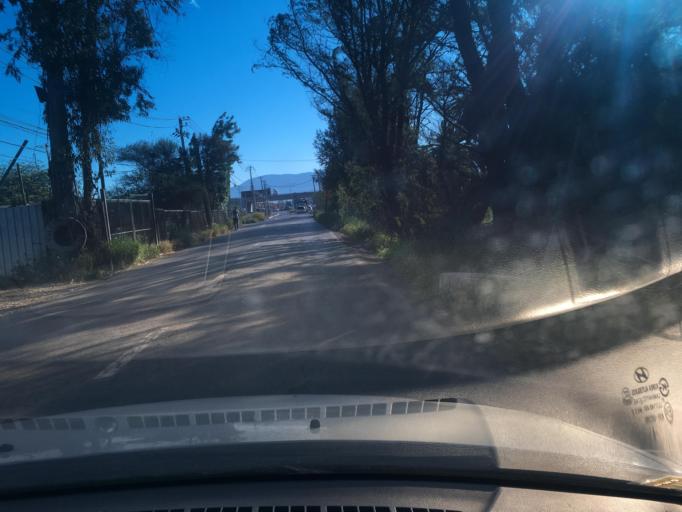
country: CL
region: Santiago Metropolitan
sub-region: Provincia de Chacabuco
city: Chicureo Abajo
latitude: -33.3123
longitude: -70.7208
